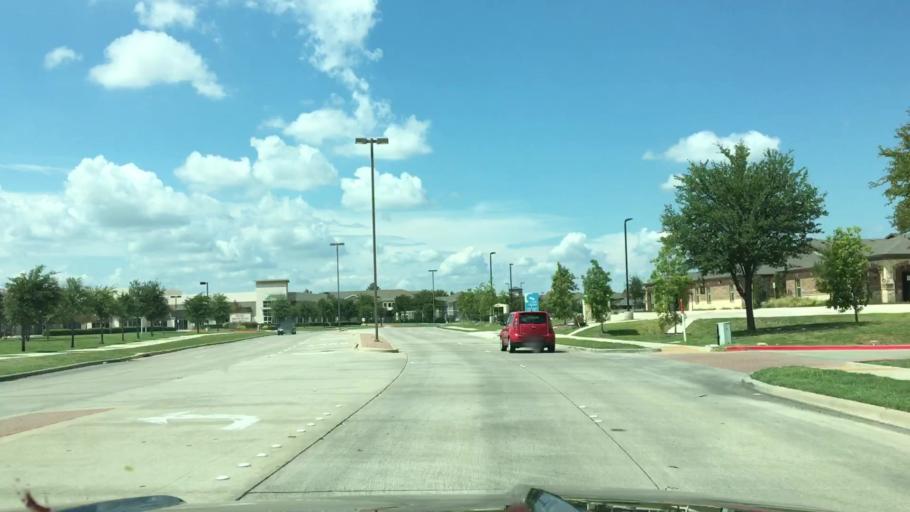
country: US
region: Texas
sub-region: Tarrant County
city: Keller
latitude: 32.9355
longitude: -97.2395
